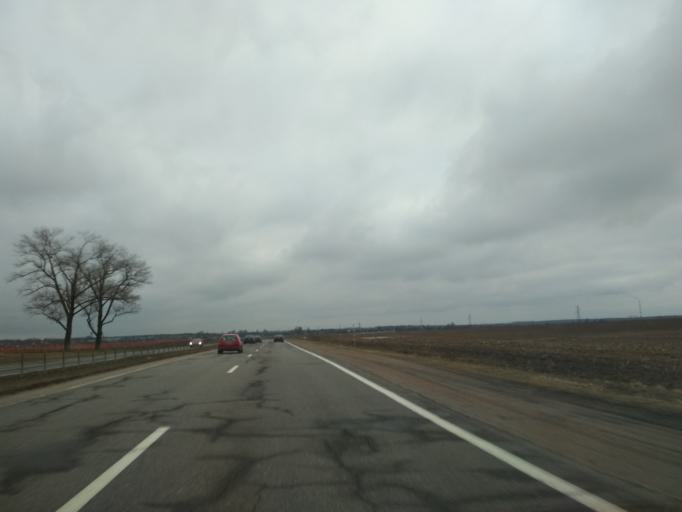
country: BY
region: Minsk
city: Dukora
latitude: 53.6812
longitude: 27.9209
